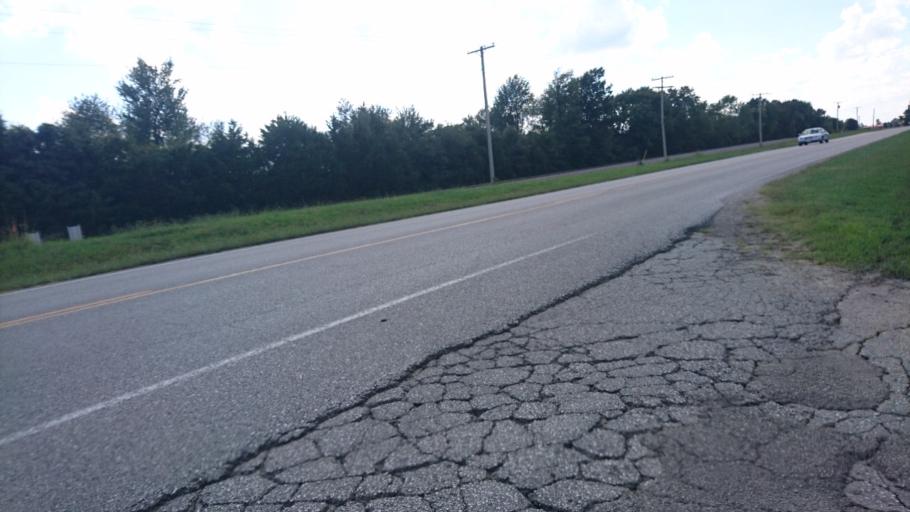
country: US
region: Missouri
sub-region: Greene County
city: Strafford
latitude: 37.2697
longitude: -93.1083
